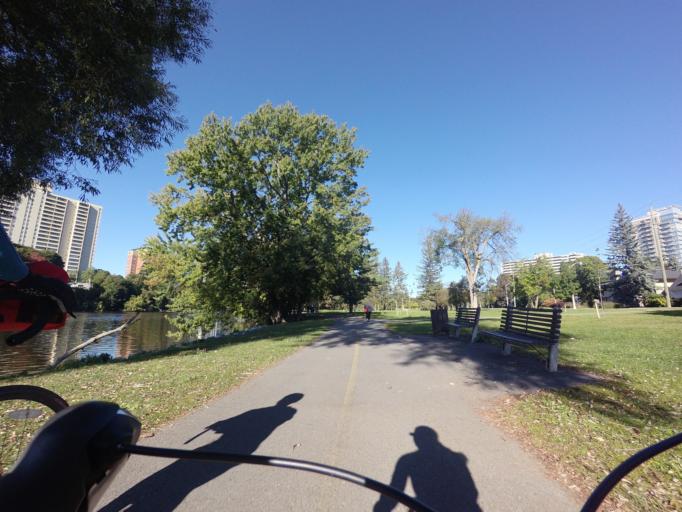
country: CA
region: Ontario
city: Ottawa
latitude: 45.4353
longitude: -75.6717
